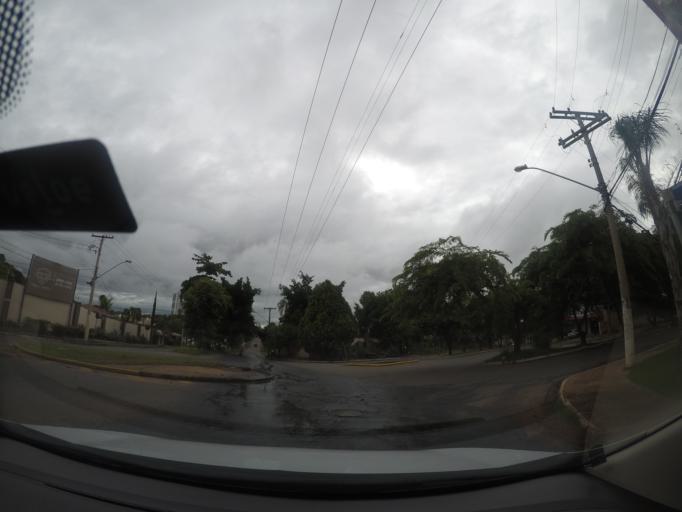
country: BR
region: Goias
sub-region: Goiania
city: Goiania
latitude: -16.7315
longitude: -49.2841
